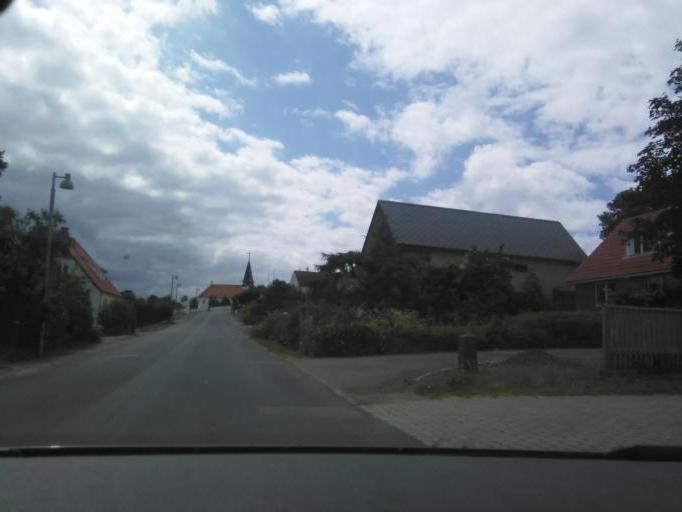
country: DK
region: Zealand
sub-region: Kalundborg Kommune
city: Gorlev
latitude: 55.5272
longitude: 11.1125
